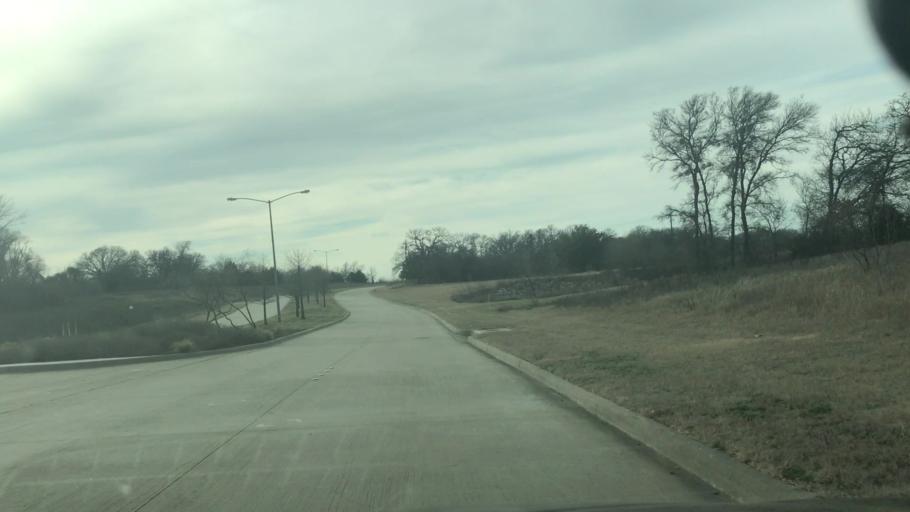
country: US
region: Texas
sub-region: Dallas County
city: Coppell
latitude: 32.9976
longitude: -97.0178
